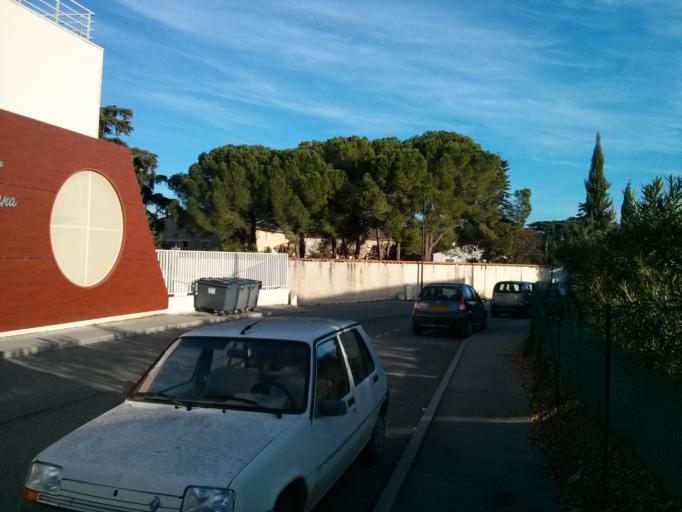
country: FR
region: Languedoc-Roussillon
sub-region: Departement du Gard
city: Aigues-Vives
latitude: 43.7383
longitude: 4.1779
